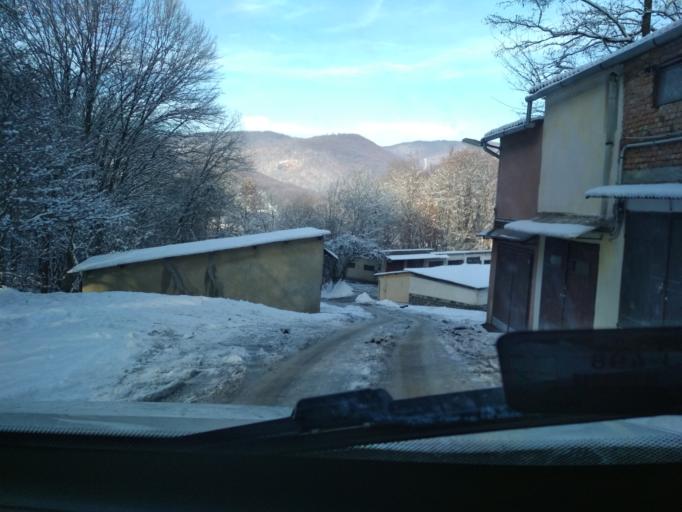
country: HU
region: Nograd
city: Salgotarjan
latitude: 48.1239
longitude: 19.8155
